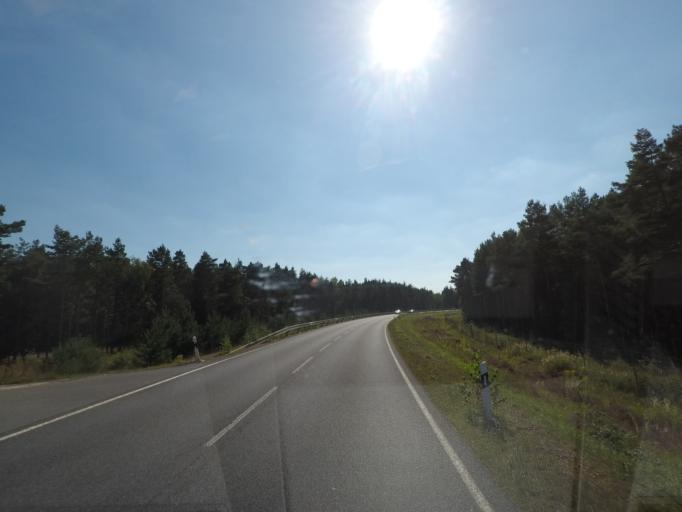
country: DE
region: Brandenburg
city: Schipkau
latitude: 51.5042
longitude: 13.9085
